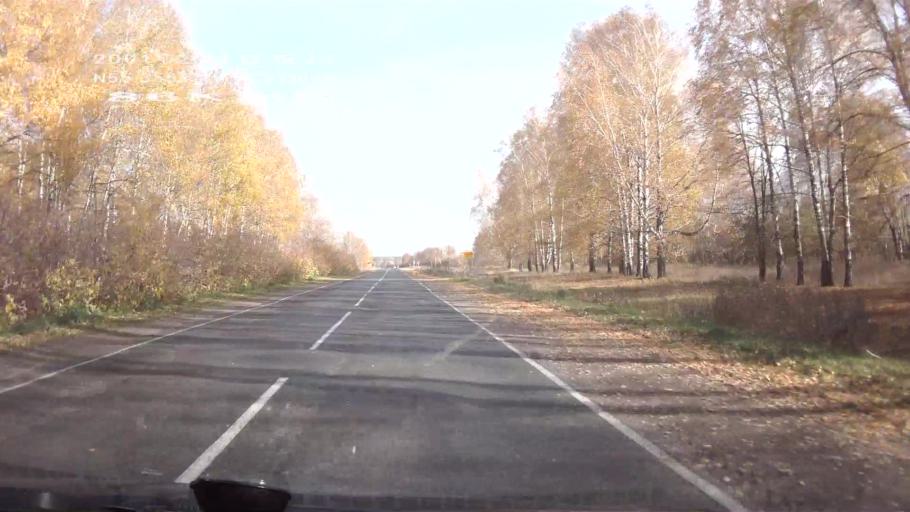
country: RU
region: Chuvashia
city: Ibresi
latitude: 55.3553
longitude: 47.2133
